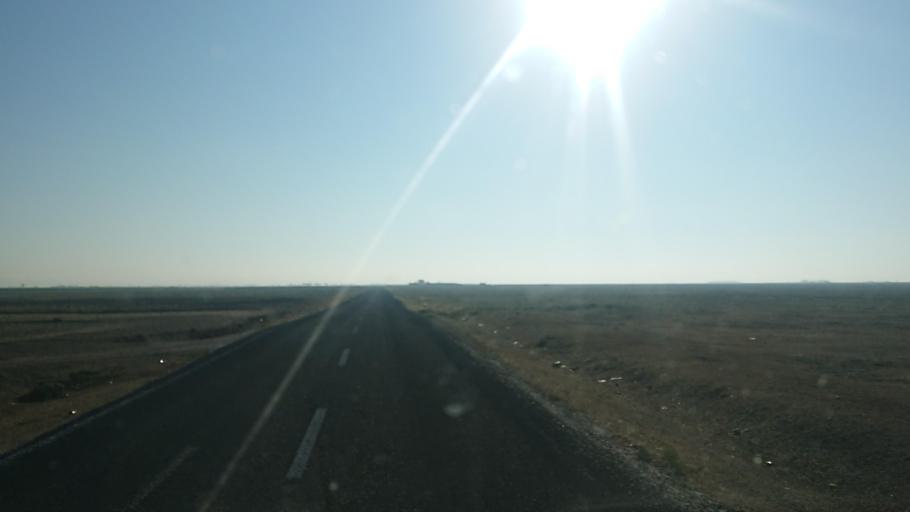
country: TR
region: Aksaray
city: Yesilova
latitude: 38.3877
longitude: 33.7948
